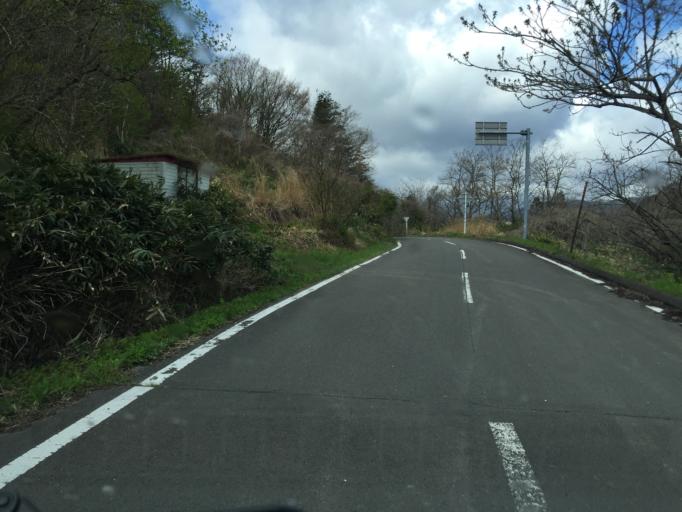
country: JP
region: Fukushima
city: Fukushima-shi
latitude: 37.8340
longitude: 140.4395
